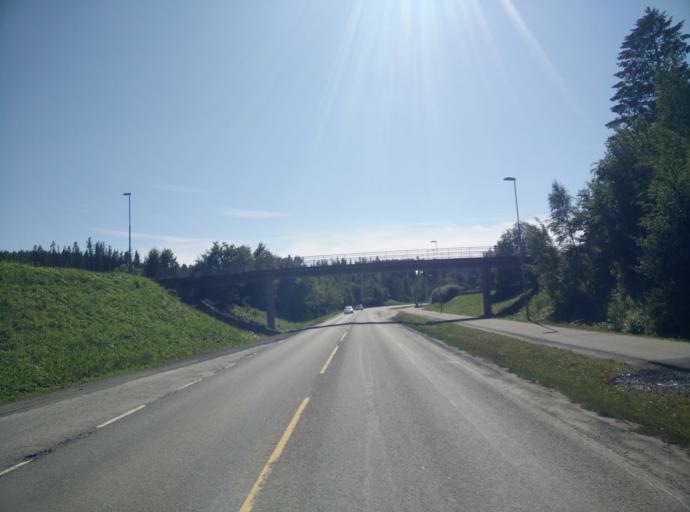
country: NO
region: Sor-Trondelag
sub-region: Trondheim
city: Trondheim
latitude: 63.3847
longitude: 10.3237
